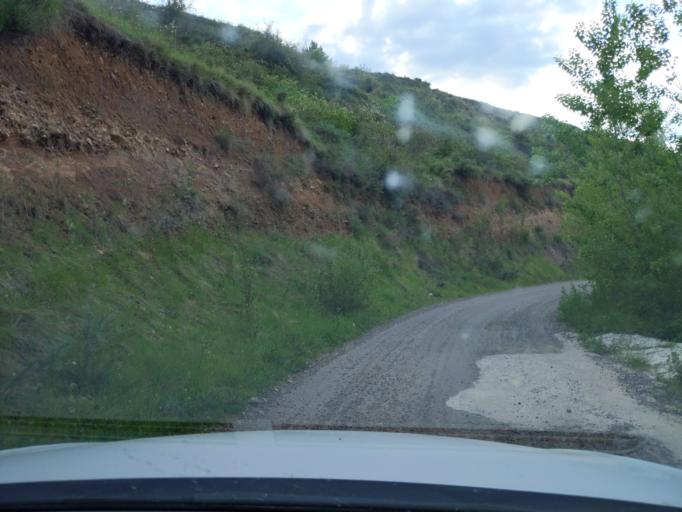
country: ES
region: La Rioja
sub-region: Provincia de La Rioja
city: Nalda
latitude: 42.3313
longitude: -2.4825
